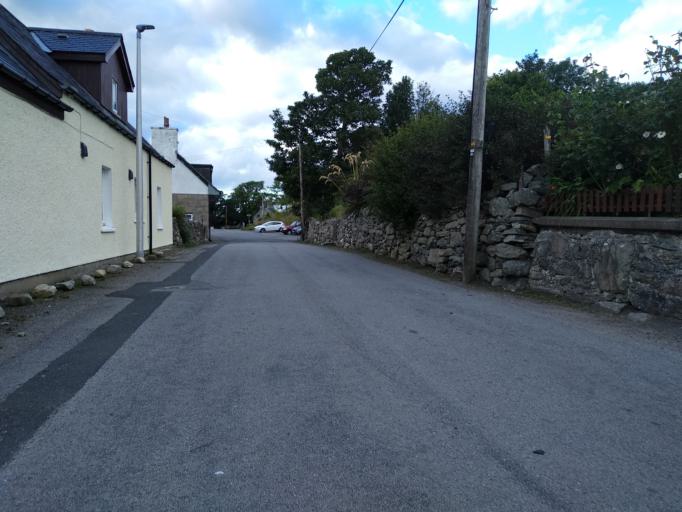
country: GB
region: Scotland
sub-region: Highland
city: Golspie
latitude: 58.4749
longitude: -4.4169
